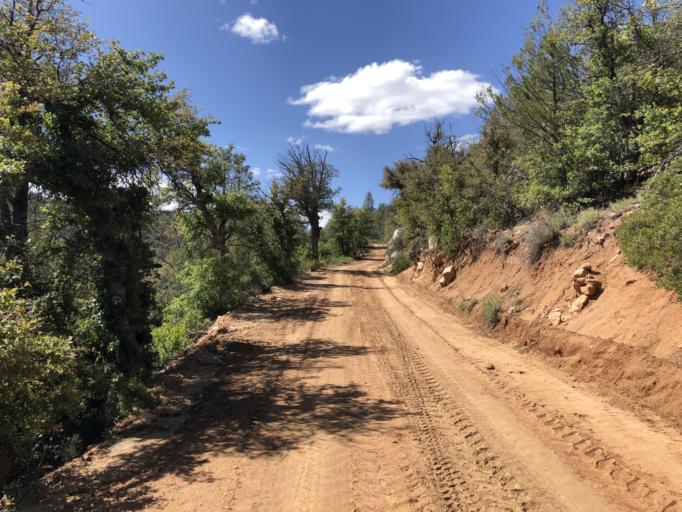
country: US
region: Arizona
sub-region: Gila County
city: Star Valley
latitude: 34.3542
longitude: -111.2795
